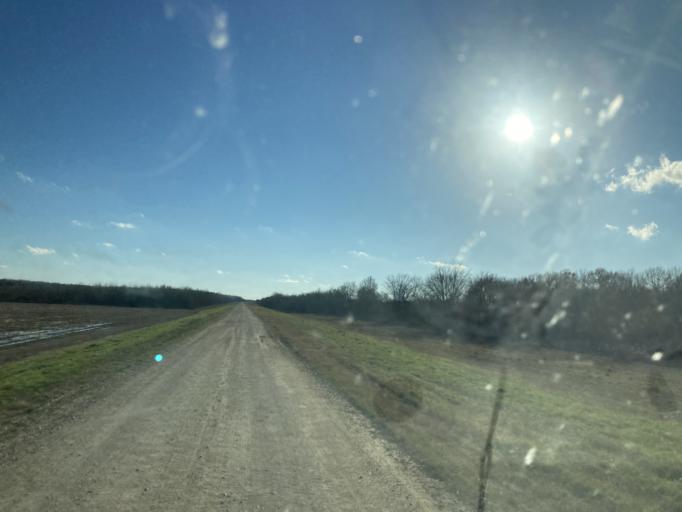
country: US
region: Mississippi
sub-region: Yazoo County
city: Yazoo City
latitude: 32.9326
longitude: -90.5480
